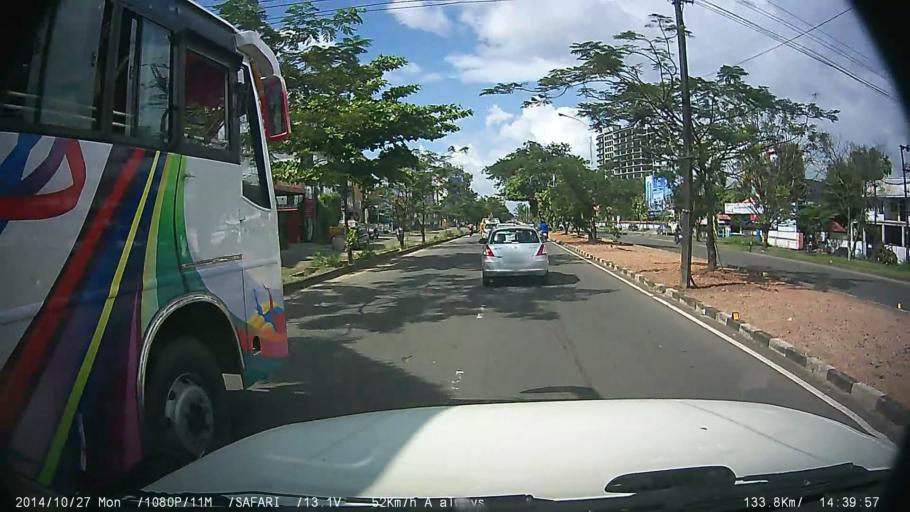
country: IN
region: Kerala
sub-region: Ernakulam
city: Cochin
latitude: 9.9939
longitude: 76.3148
